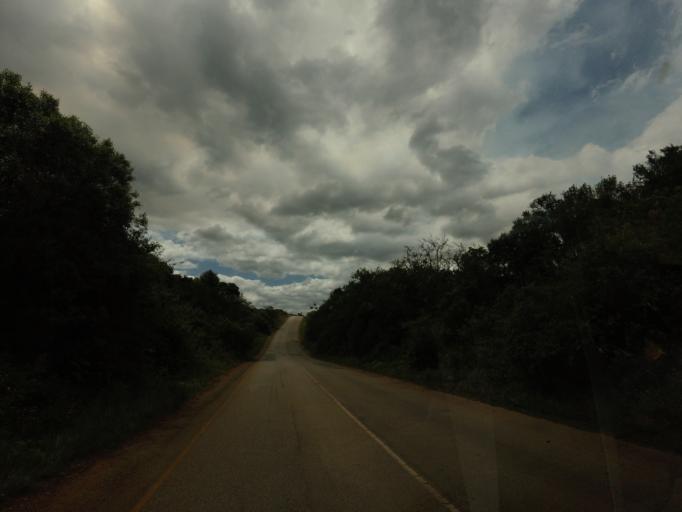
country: ZA
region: Mpumalanga
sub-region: Ehlanzeni District
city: Graksop
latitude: -24.9296
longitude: 30.8102
